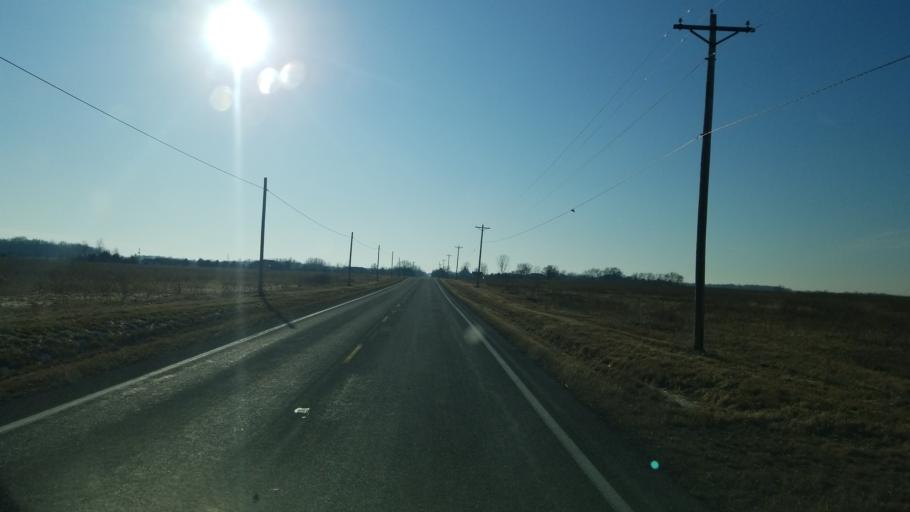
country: US
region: Ohio
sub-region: Sandusky County
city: Green Springs
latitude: 41.2458
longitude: -82.9957
